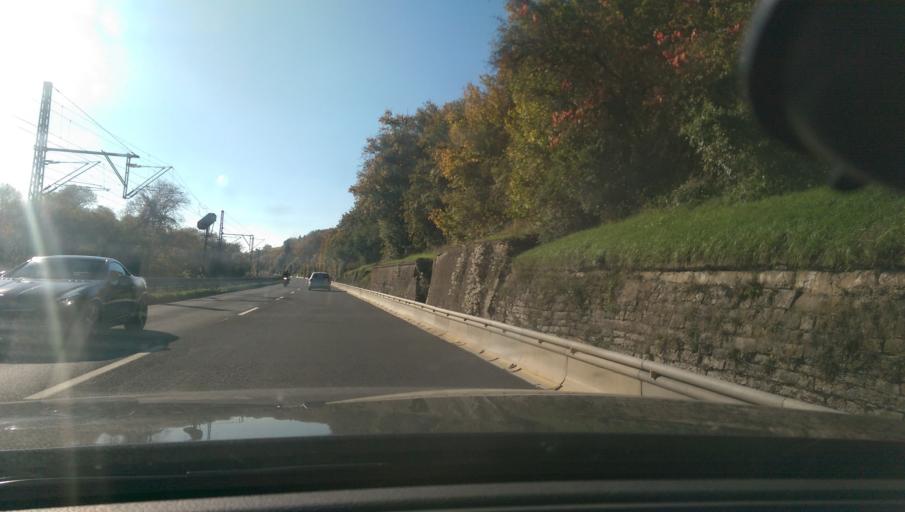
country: DE
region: Bavaria
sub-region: Regierungsbezirk Unterfranken
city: Sennfeld
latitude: 50.0564
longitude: 10.2686
